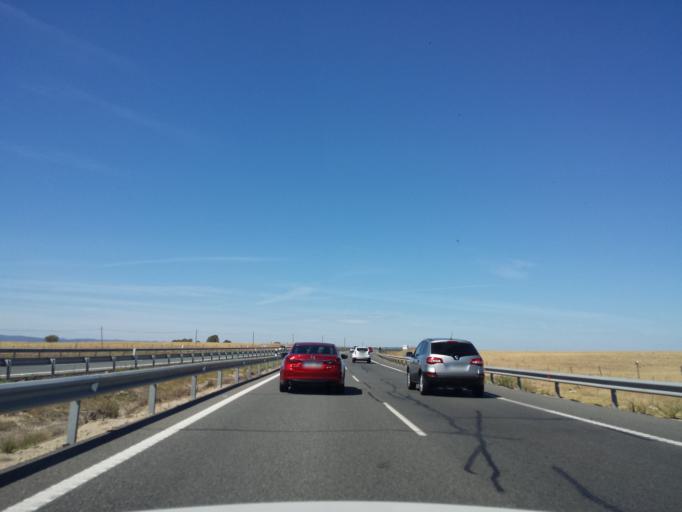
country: ES
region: Extremadura
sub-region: Provincia de Caceres
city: Berrocalejo
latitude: 39.8936
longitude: -5.3662
